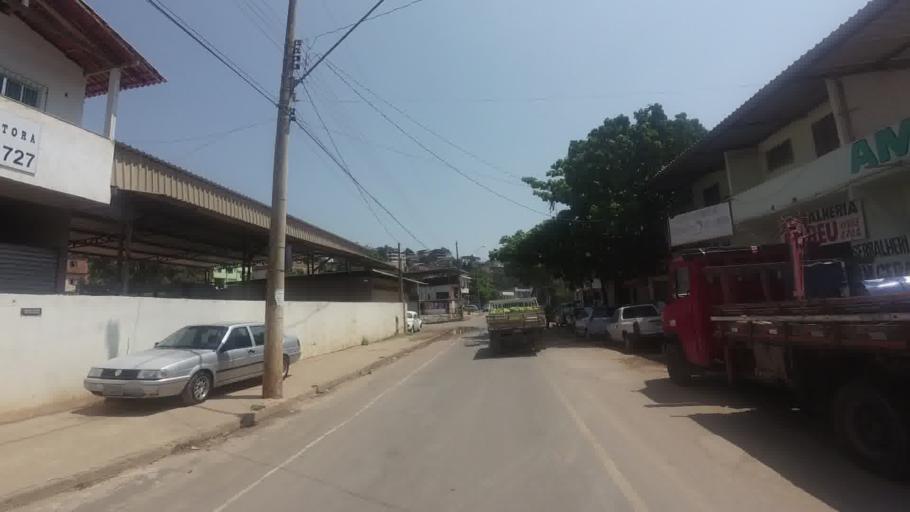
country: BR
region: Espirito Santo
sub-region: Cachoeiro De Itapemirim
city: Cachoeiro de Itapemirim
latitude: -20.8498
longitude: -41.1005
